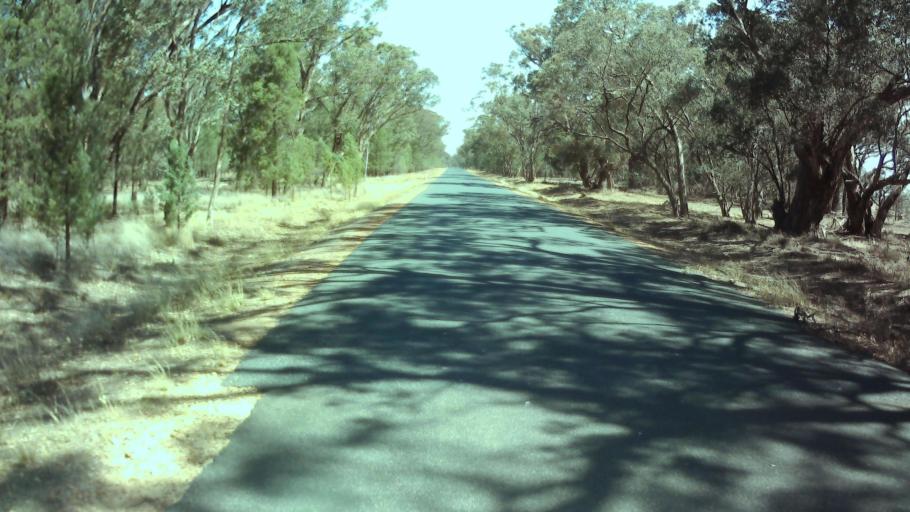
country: AU
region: New South Wales
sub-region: Weddin
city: Grenfell
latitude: -34.0281
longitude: 148.1329
